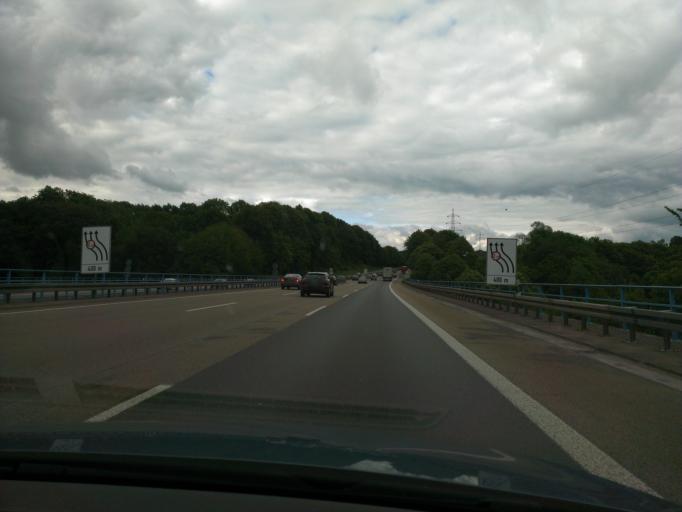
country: DE
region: North Rhine-Westphalia
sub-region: Regierungsbezirk Koln
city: Odenthal
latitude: 51.0660
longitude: 7.0769
